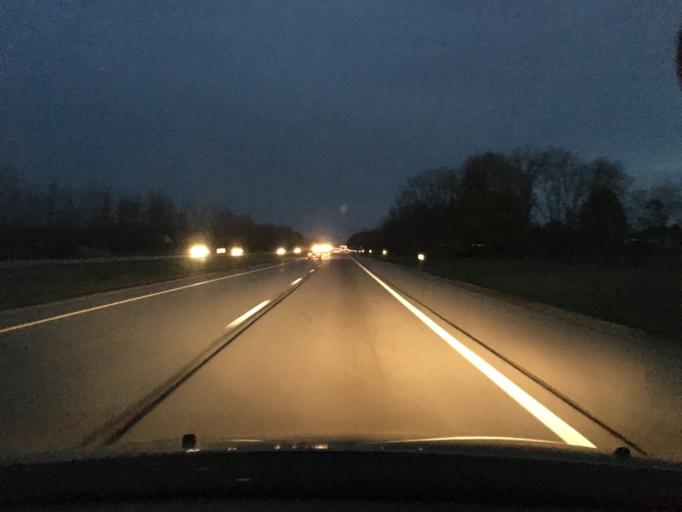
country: US
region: New York
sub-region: Ontario County
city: Manchester
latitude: 42.9858
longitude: -77.3012
